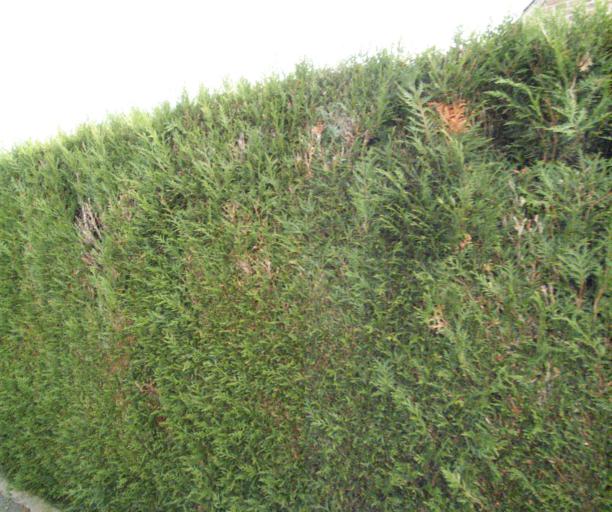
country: FR
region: Nord-Pas-de-Calais
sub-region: Departement du Nord
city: Wattignies
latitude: 50.5857
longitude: 3.0418
